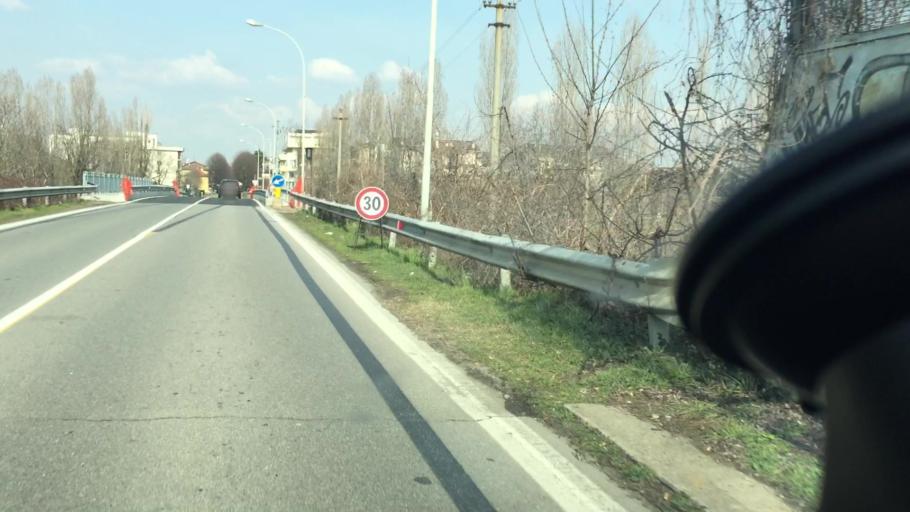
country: IT
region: Lombardy
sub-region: Citta metropolitana di Milano
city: Cernusco sul Naviglio
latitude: 45.5213
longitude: 9.3379
